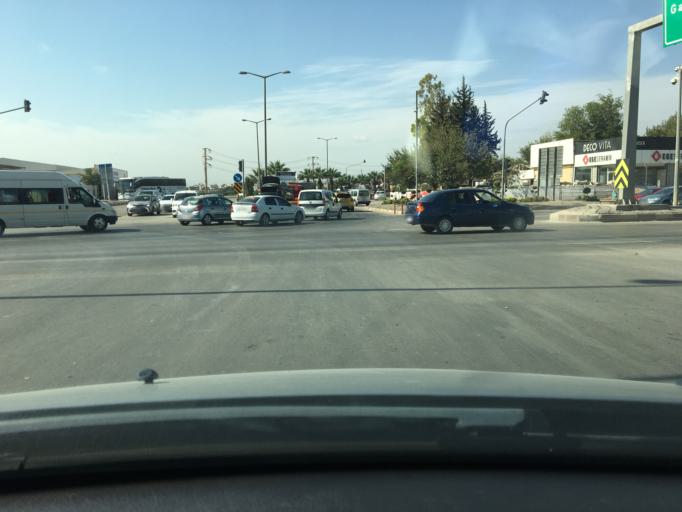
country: TR
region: Adana
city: Seyhan
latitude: 37.0236
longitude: 35.2541
